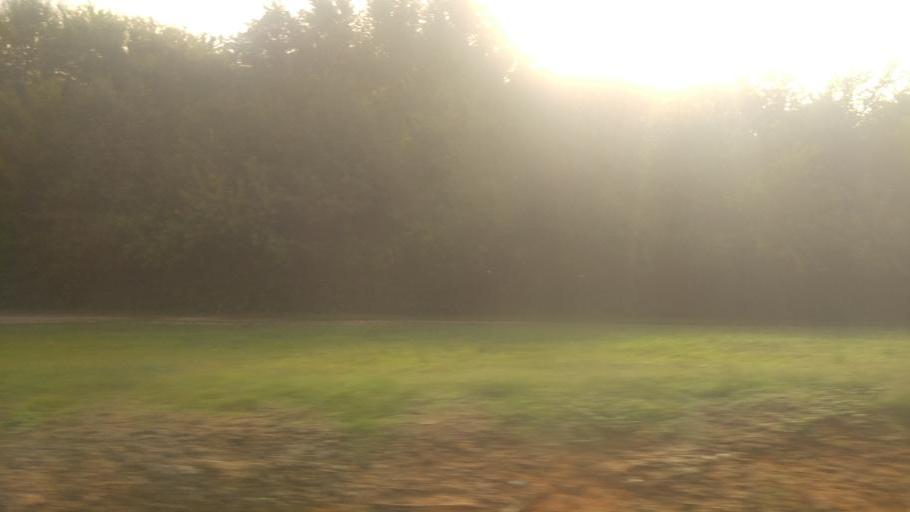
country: US
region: North Carolina
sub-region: Wake County
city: Raleigh
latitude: 35.7628
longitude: -78.6372
